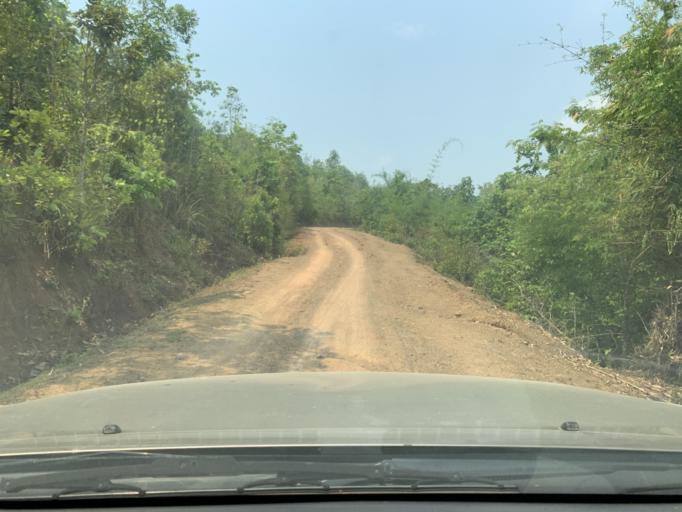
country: LA
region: Louangphabang
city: Louangphabang
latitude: 19.9391
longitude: 102.1386
